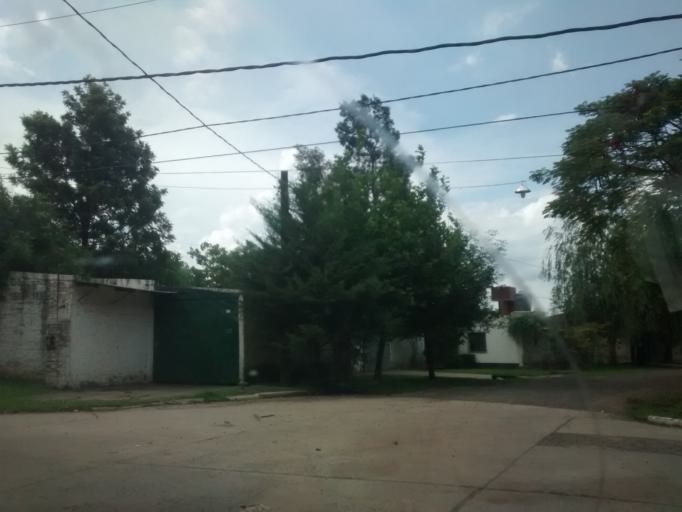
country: AR
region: Chaco
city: Resistencia
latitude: -27.4324
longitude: -58.9795
